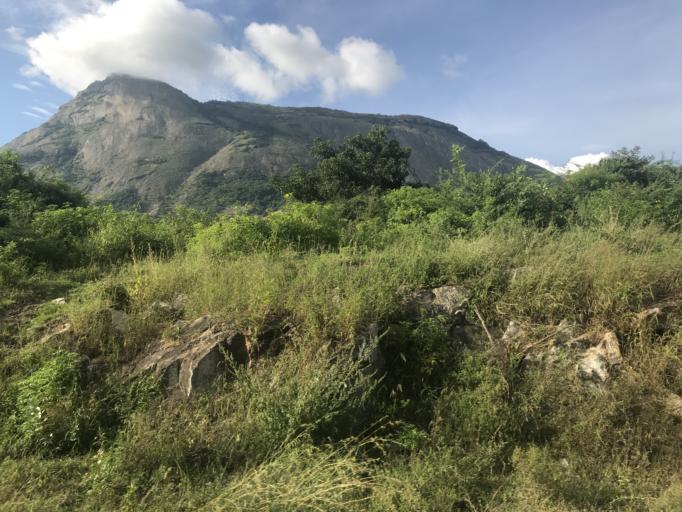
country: IN
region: Tamil Nadu
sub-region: Coimbatore
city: Madukkarai
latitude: 10.8973
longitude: 76.8911
